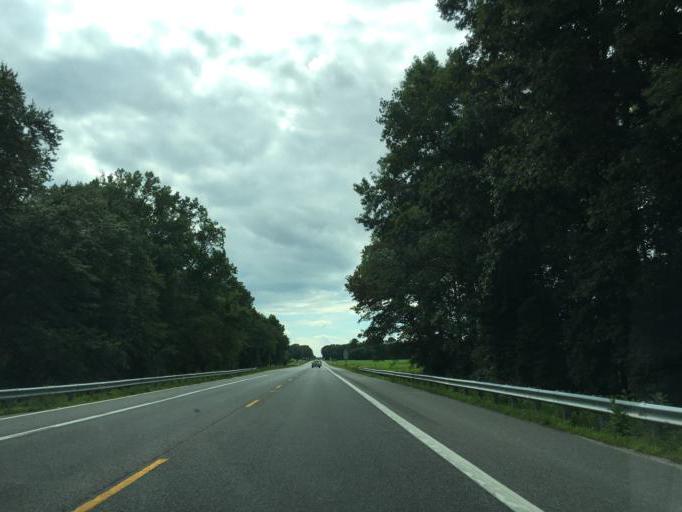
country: US
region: Maryland
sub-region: Caroline County
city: Ridgely
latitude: 38.9179
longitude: -75.9091
